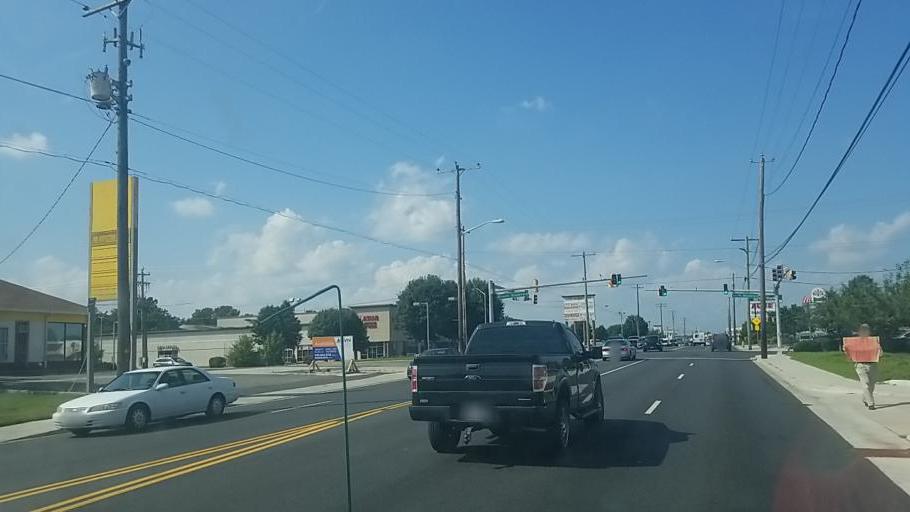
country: US
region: Maryland
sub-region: Wicomico County
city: Salisbury
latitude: 38.3531
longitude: -75.6010
